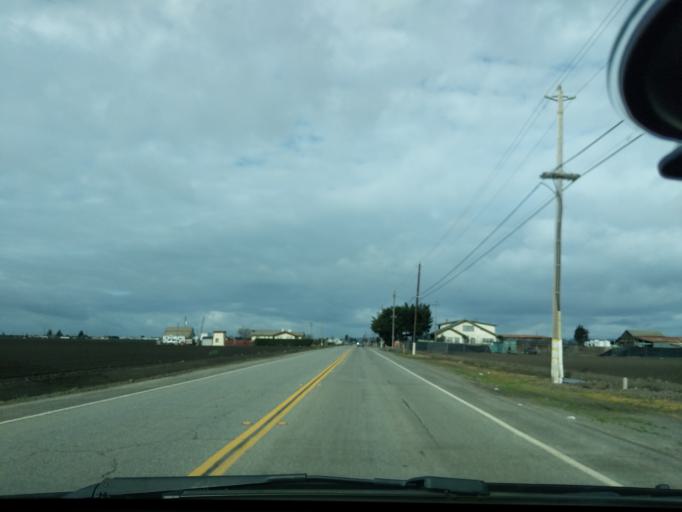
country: US
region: California
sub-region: Monterey County
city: Pajaro
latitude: 36.9041
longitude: -121.7216
